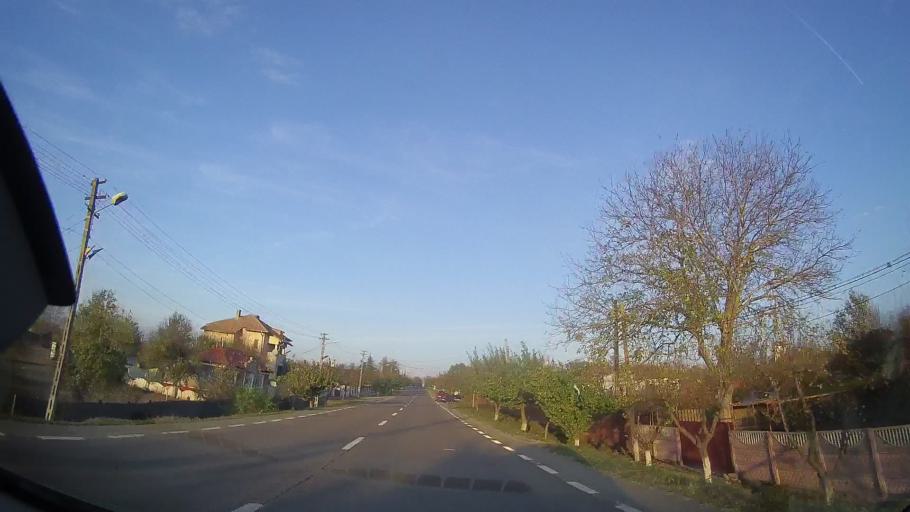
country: RO
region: Constanta
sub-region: Comuna Comana
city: Comana
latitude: 43.8943
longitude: 28.3163
